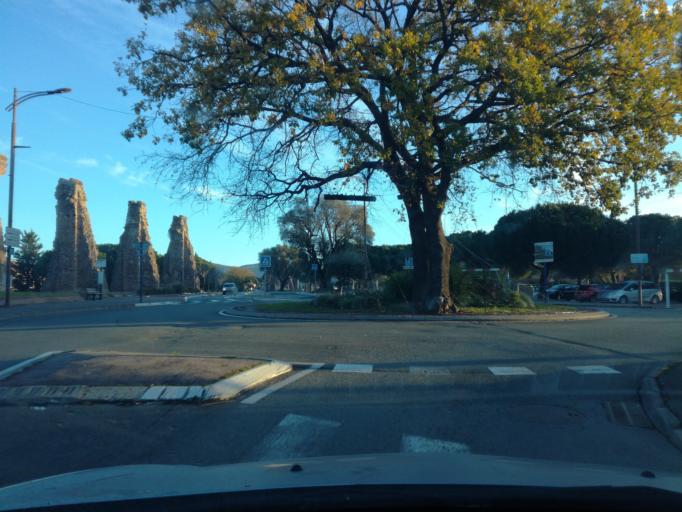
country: FR
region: Provence-Alpes-Cote d'Azur
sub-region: Departement du Var
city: Frejus
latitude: 43.4371
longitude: 6.7408
